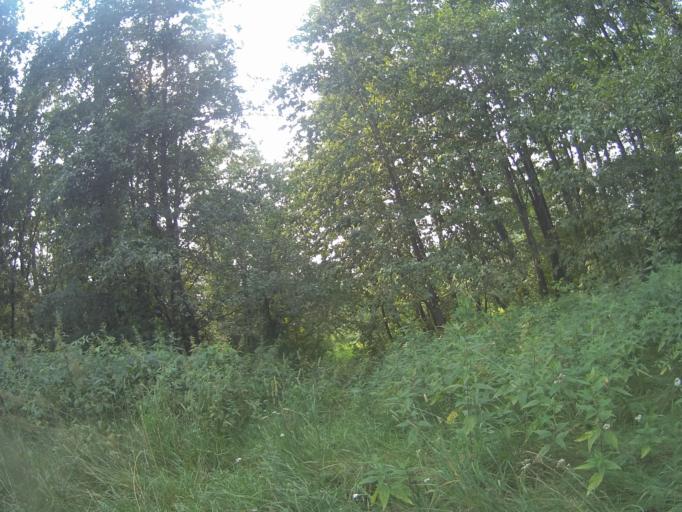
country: RU
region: Vladimir
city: Vorsha
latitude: 56.0209
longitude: 40.1471
